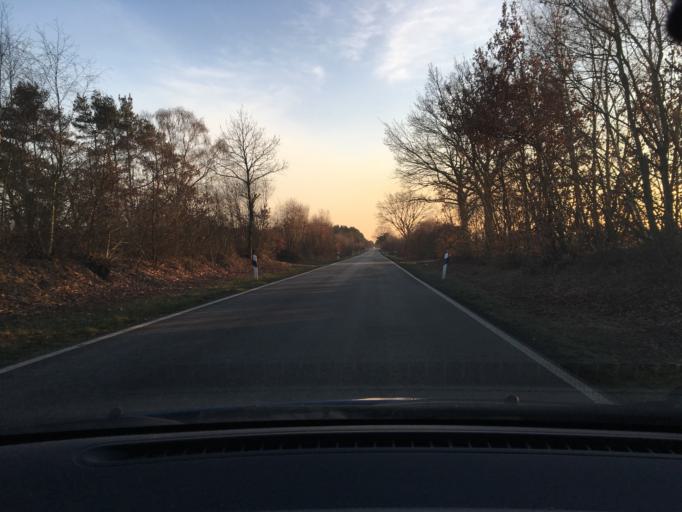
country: DE
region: Schleswig-Holstein
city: Besenthal
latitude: 53.5236
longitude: 10.7461
